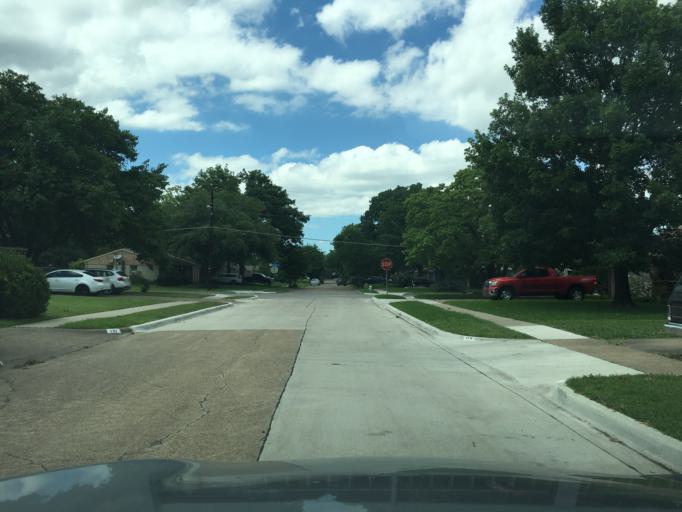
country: US
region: Texas
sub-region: Dallas County
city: Richardson
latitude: 32.9497
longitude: -96.7111
